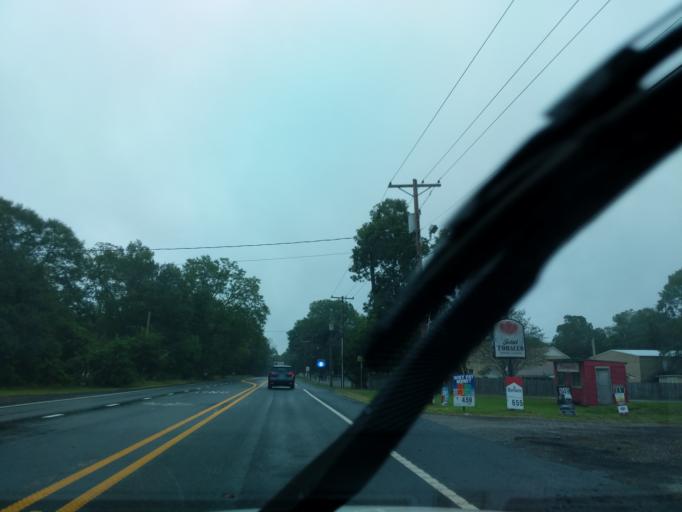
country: US
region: Louisiana
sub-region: Caddo Parish
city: Greenwood
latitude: 32.3734
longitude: -94.0418
